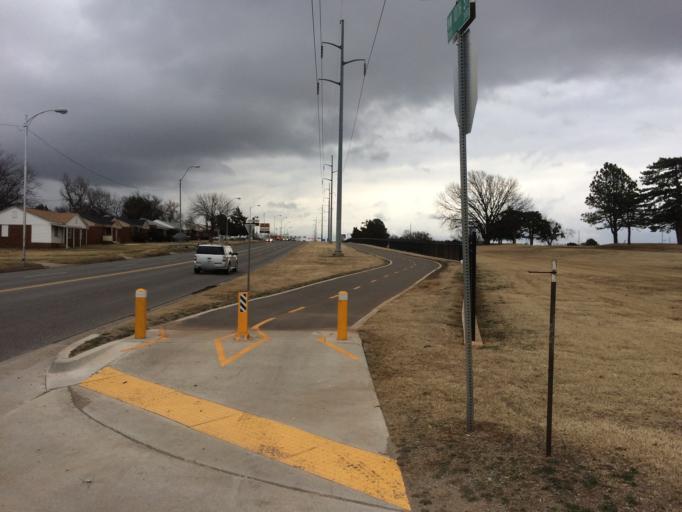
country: US
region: Oklahoma
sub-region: Oklahoma County
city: Oklahoma City
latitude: 35.4785
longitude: -97.5702
